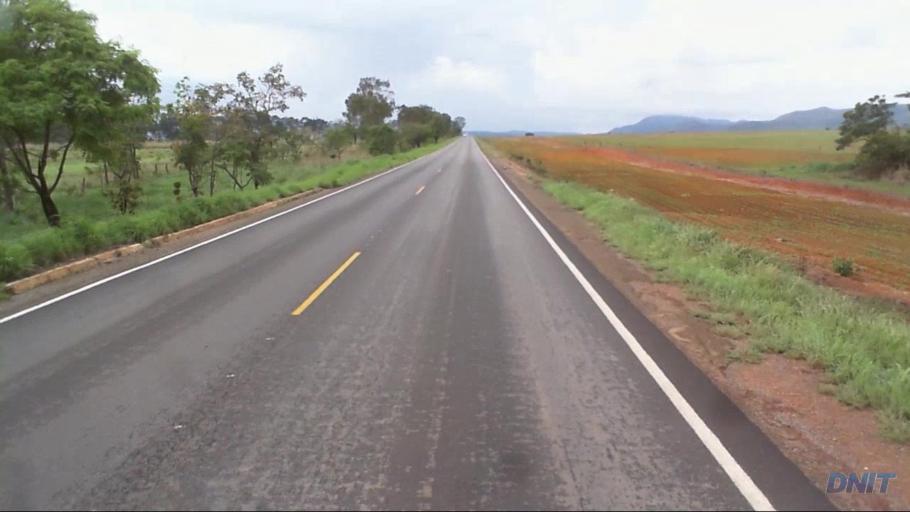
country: BR
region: Goias
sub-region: Padre Bernardo
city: Padre Bernardo
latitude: -15.3134
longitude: -48.2281
